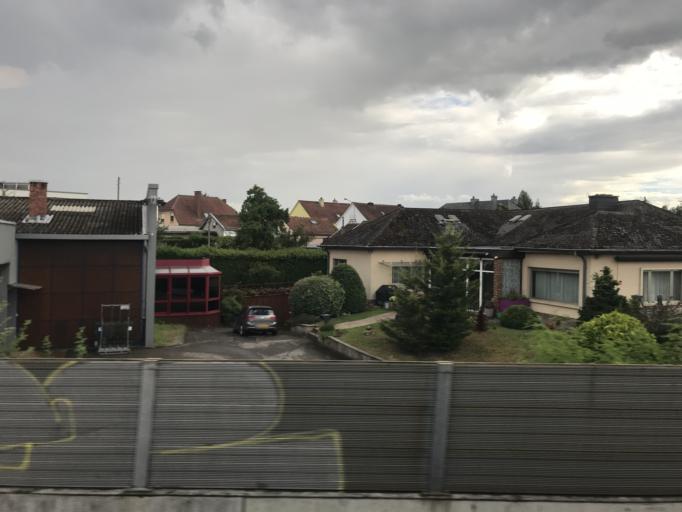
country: LU
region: Luxembourg
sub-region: Canton de Luxembourg
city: Luxembourg
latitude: 49.5965
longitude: 6.1084
